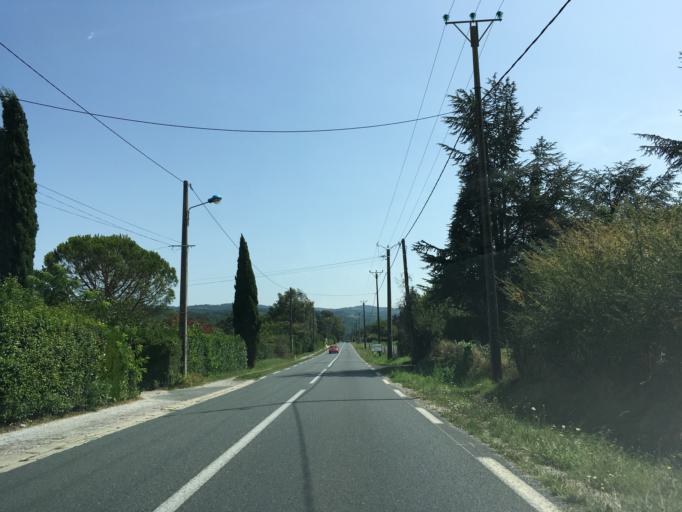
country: FR
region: Midi-Pyrenees
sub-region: Departement du Tarn
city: Castres
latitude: 43.6214
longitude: 2.2755
